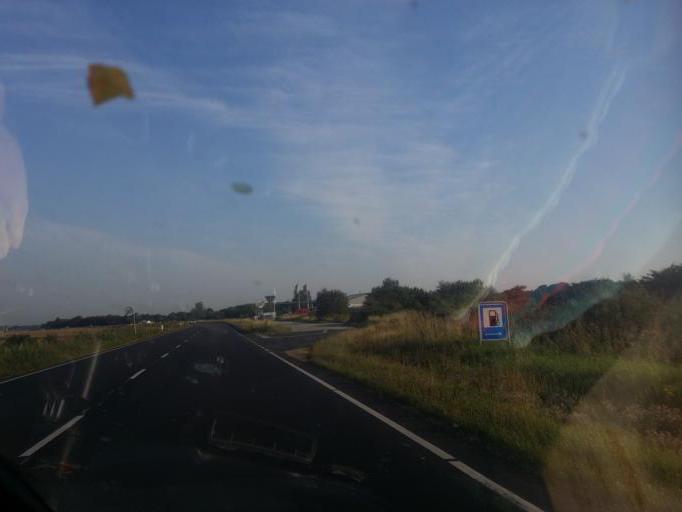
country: DE
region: Schleswig-Holstein
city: Suderlugum
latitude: 54.9079
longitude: 8.9081
